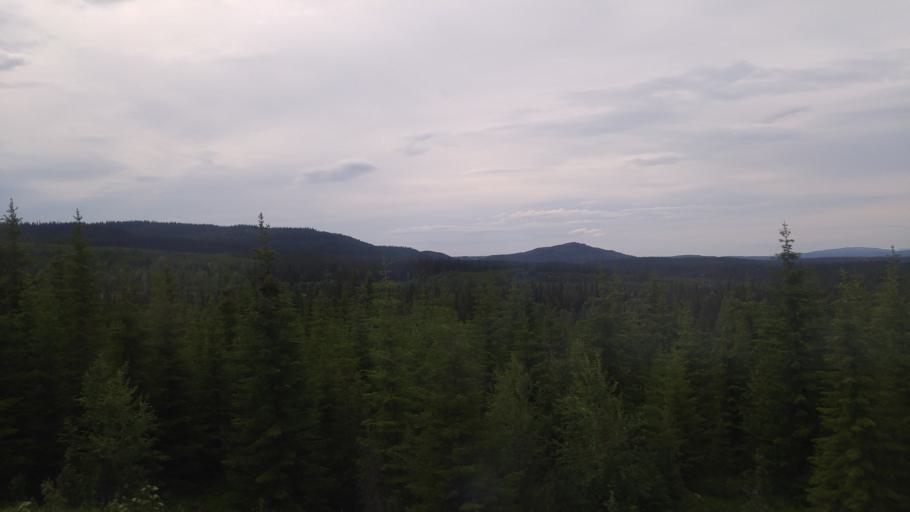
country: SE
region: Jaemtland
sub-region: Are Kommun
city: Are
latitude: 63.3937
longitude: 12.7958
